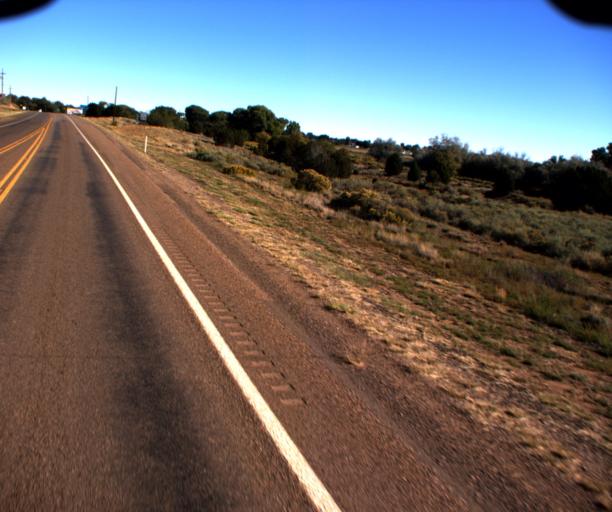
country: US
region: Arizona
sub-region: Navajo County
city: Taylor
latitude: 34.4529
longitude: -110.0918
